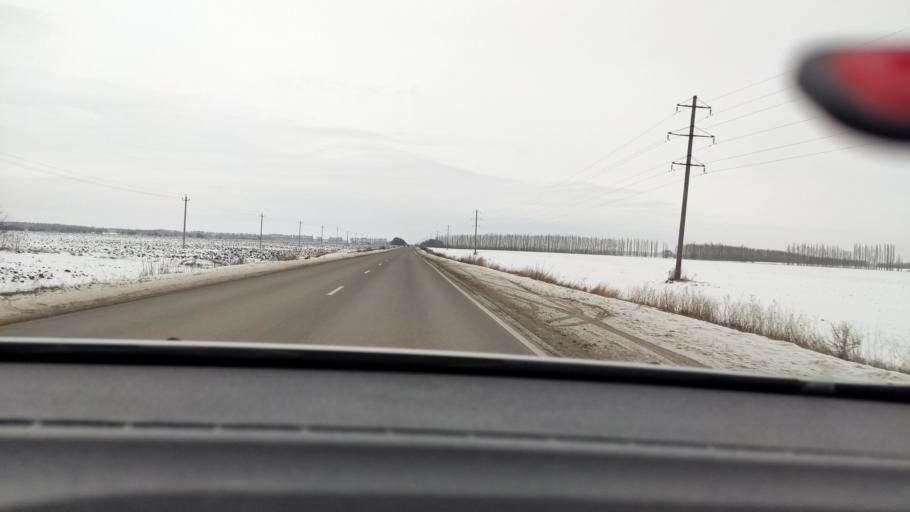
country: RU
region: Voronezj
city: Latnaya
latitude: 51.7440
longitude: 38.9373
